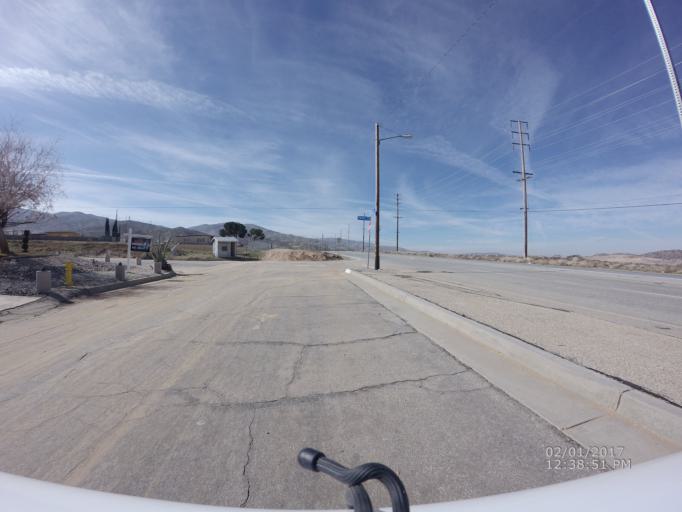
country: US
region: California
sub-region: Los Angeles County
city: Desert View Highlands
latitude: 34.5578
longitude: -118.1497
